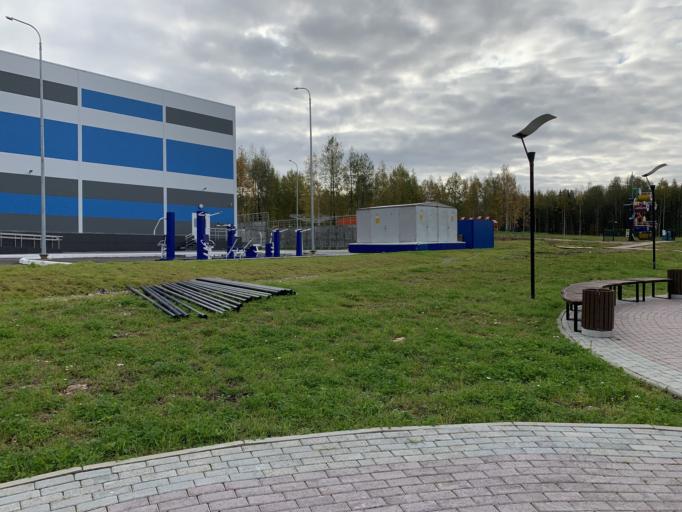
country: RU
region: Perm
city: Gubakha
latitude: 58.8336
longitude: 57.5610
